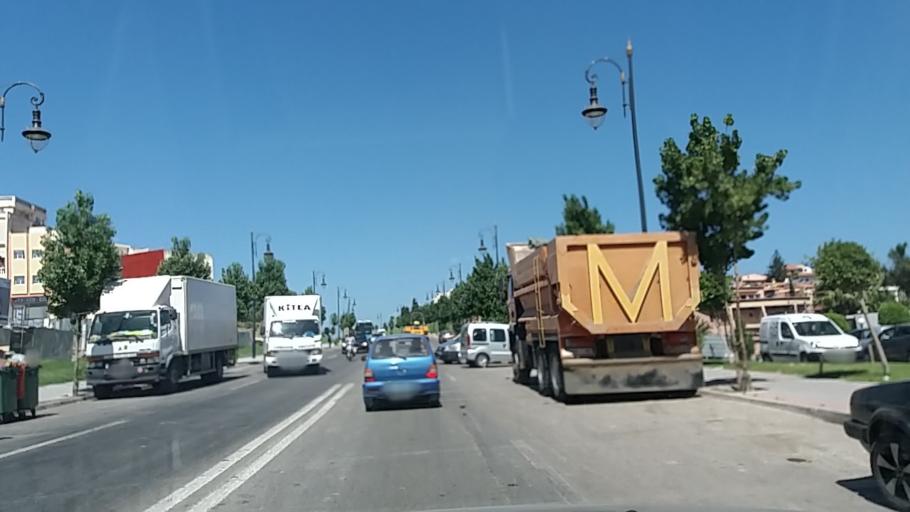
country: MA
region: Tanger-Tetouan
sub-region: Tanger-Assilah
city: Tangier
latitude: 35.7721
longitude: -5.7705
